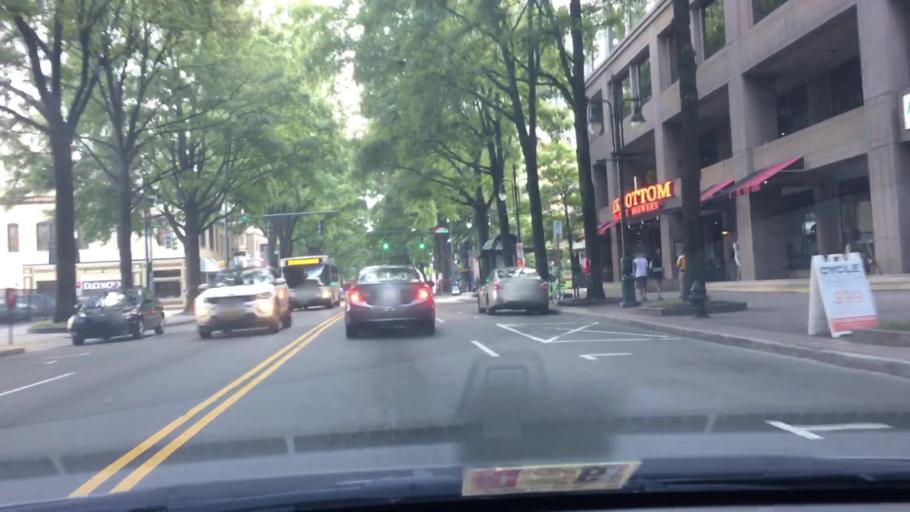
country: US
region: North Carolina
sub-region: Mecklenburg County
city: Charlotte
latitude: 35.2300
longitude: -80.8393
